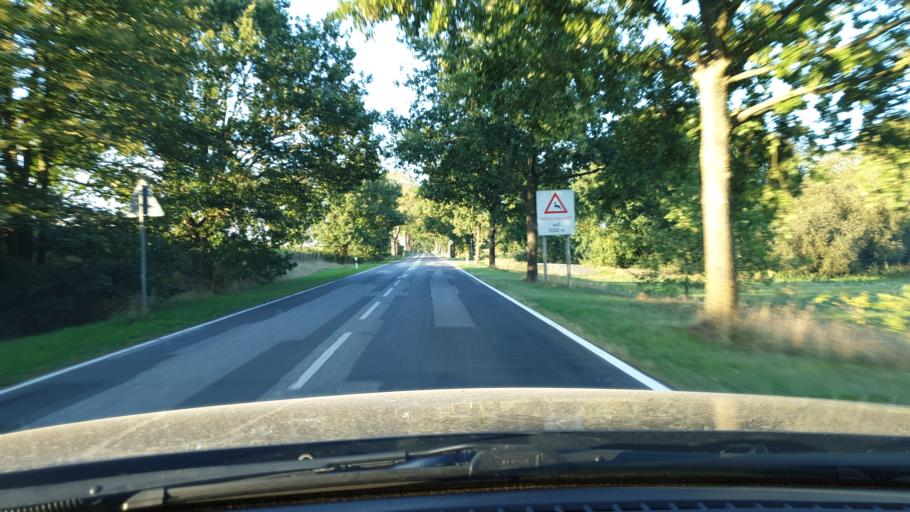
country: DE
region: Mecklenburg-Vorpommern
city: Wittenburg
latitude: 53.5452
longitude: 11.0880
